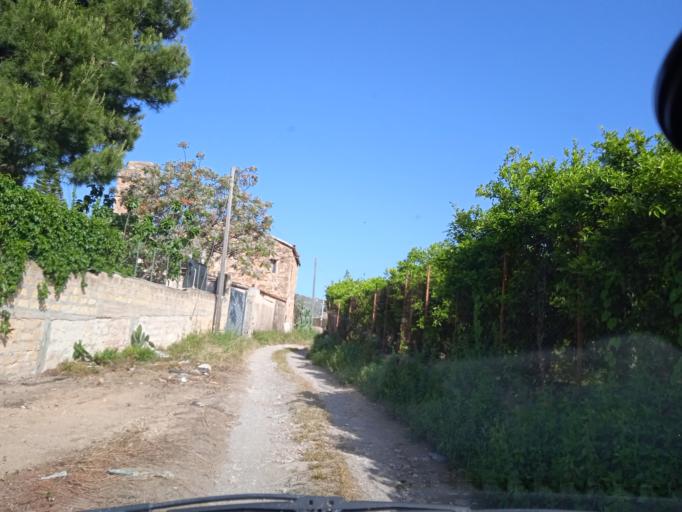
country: IT
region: Sicily
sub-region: Palermo
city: Villabate
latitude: 38.0817
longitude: 13.4517
